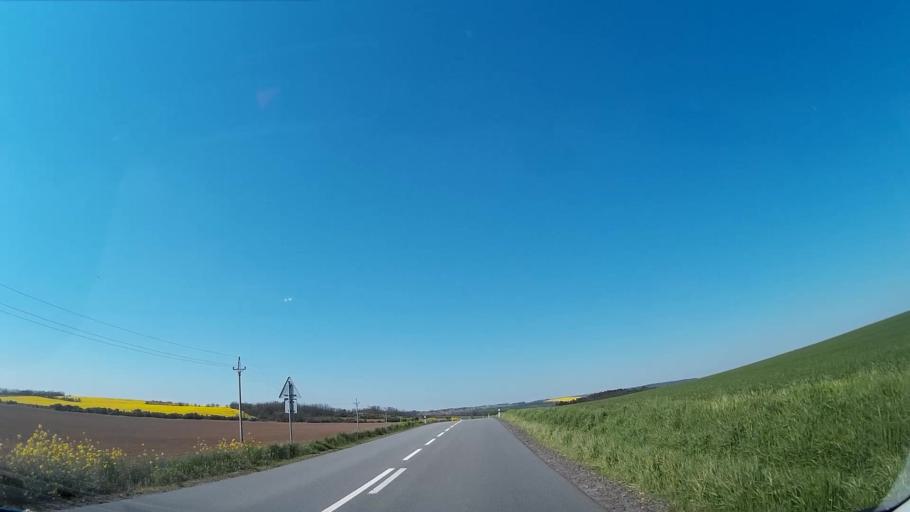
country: CZ
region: South Moravian
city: Ivancice
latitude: 49.0816
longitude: 16.3475
